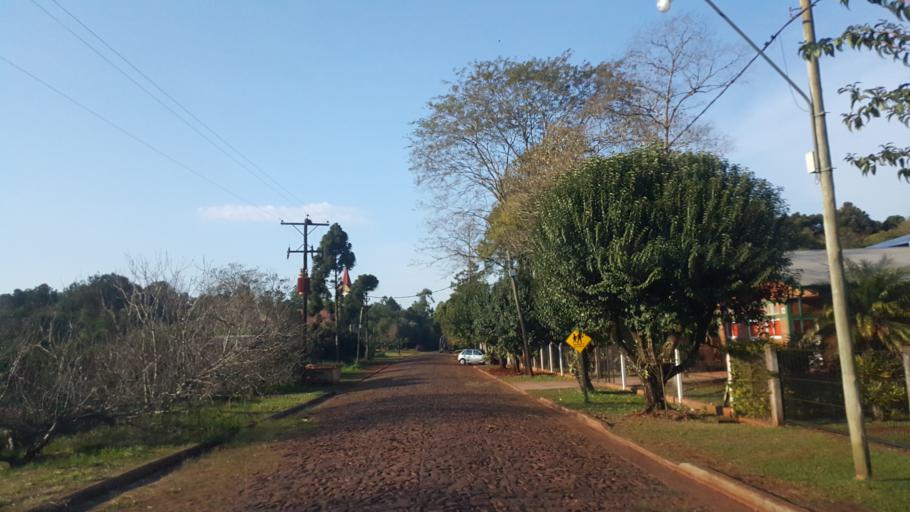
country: AR
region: Misiones
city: Capiovi
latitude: -26.8902
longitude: -55.0593
